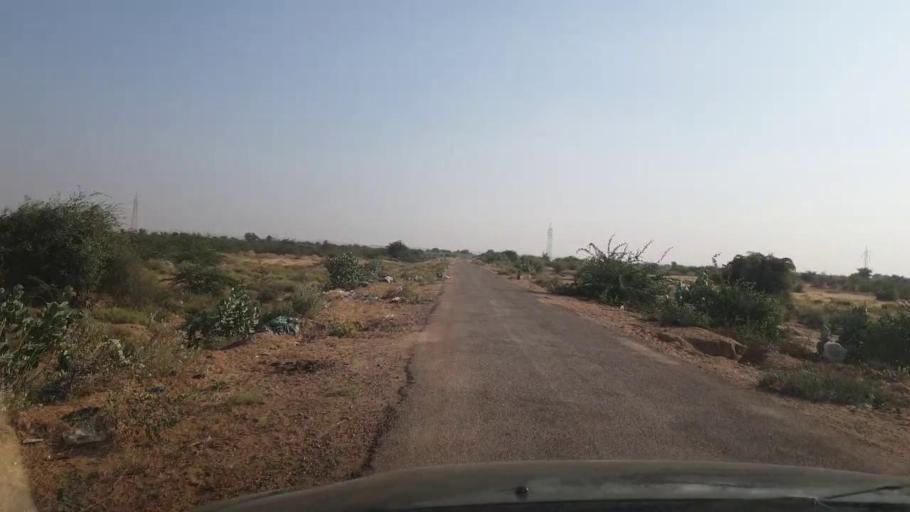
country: PK
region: Sindh
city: Jamshoro
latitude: 25.3528
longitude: 67.8364
